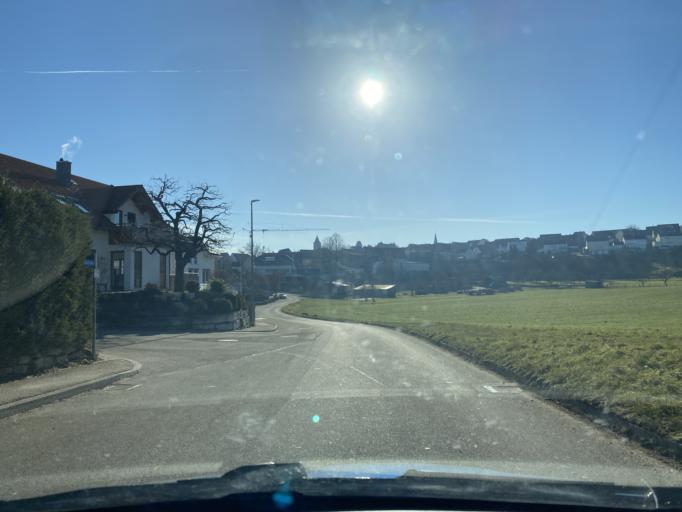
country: DE
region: Baden-Wuerttemberg
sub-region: Regierungsbezirk Stuttgart
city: Eberdingen
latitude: 48.8973
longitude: 8.9334
